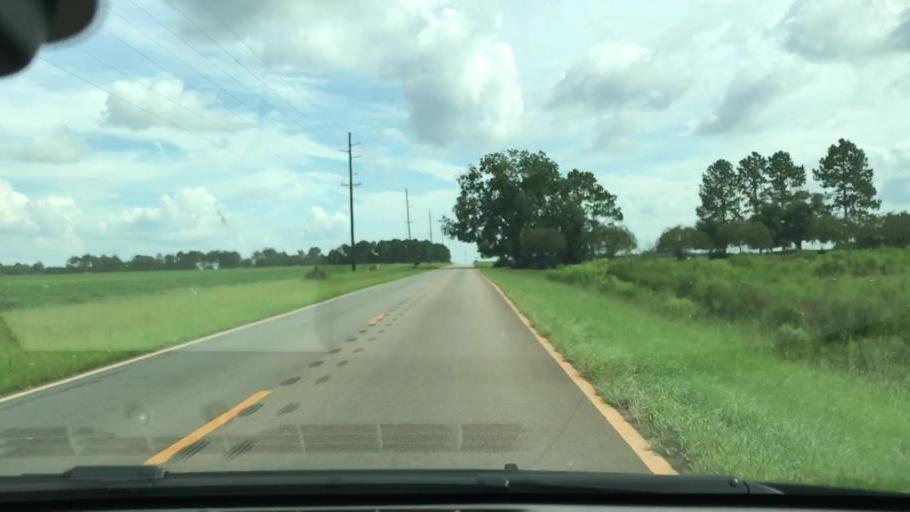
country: US
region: Georgia
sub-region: Clay County
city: Fort Gaines
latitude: 31.5382
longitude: -84.9610
